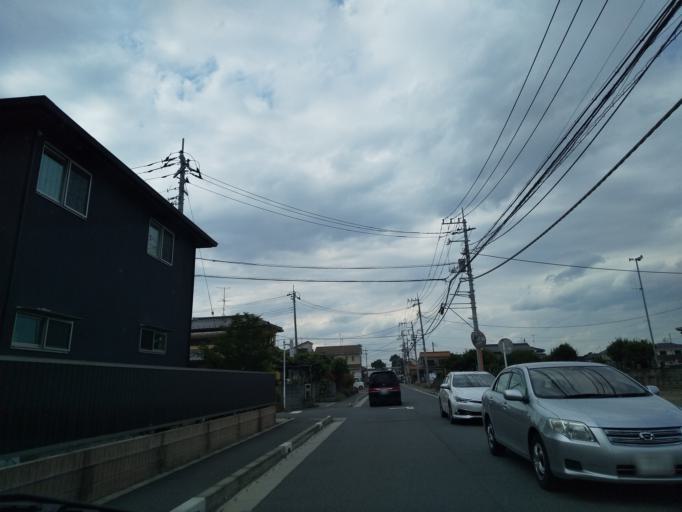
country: JP
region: Chiba
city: Noda
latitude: 35.9890
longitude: 139.8130
